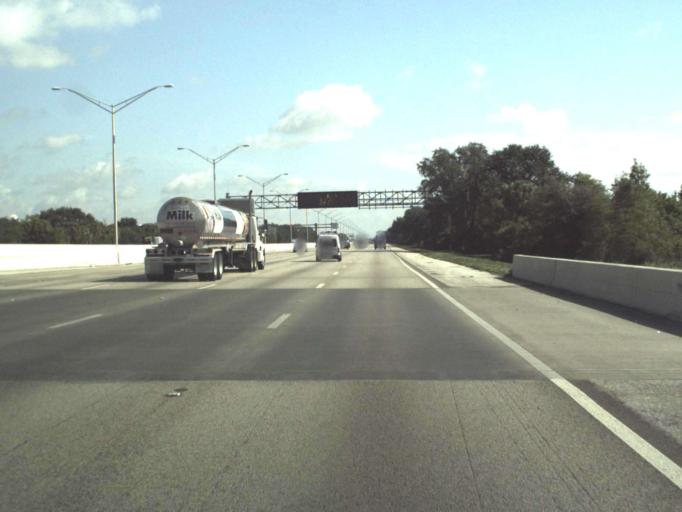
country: US
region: Florida
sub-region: Palm Beach County
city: Schall Circle
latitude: 26.7333
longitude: -80.0908
